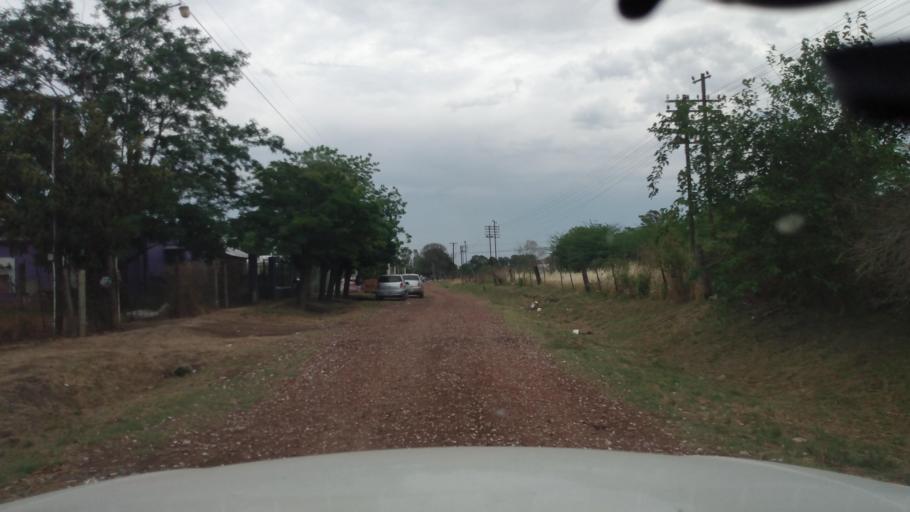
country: AR
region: Buenos Aires
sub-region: Partido de Lujan
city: Lujan
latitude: -34.5539
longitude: -59.2030
